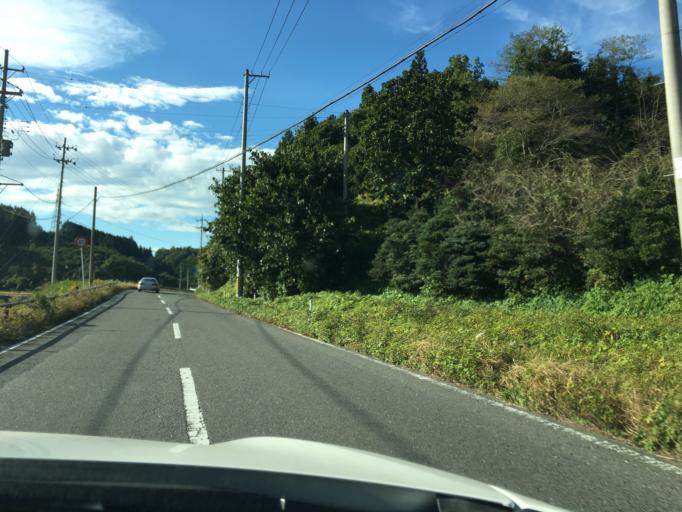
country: JP
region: Fukushima
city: Ishikawa
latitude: 37.1833
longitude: 140.4618
